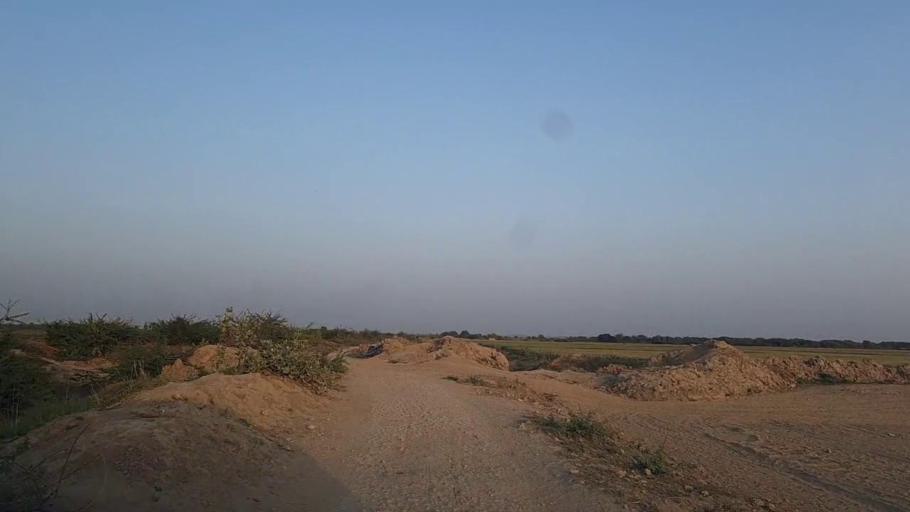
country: PK
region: Sindh
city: Naukot
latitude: 24.6967
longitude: 69.2668
